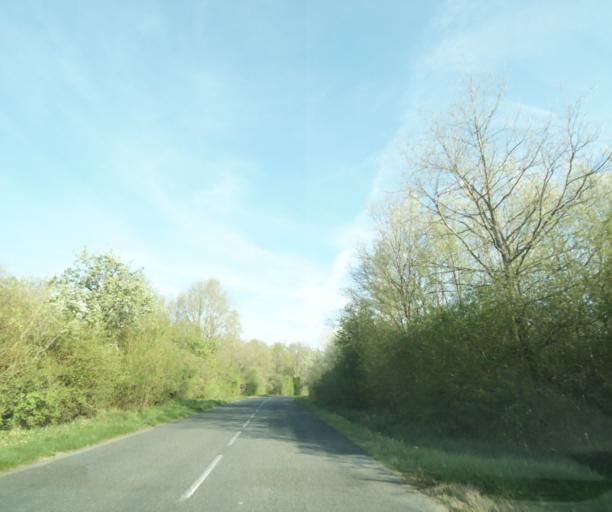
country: FR
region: Ile-de-France
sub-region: Departement de Seine-et-Marne
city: Vernou-la-Celle-sur-Seine
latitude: 48.4659
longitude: 2.8683
